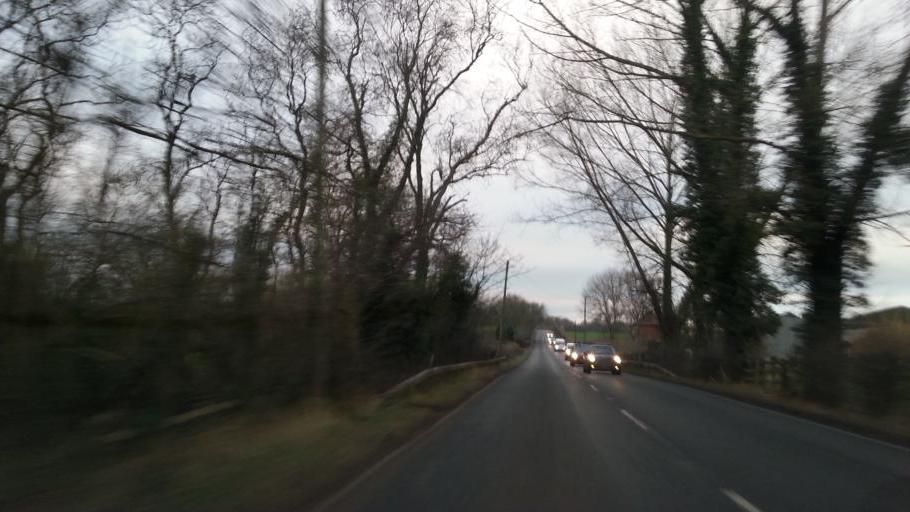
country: GB
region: England
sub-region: Nottinghamshire
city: Southwell
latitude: 53.1112
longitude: -0.9673
